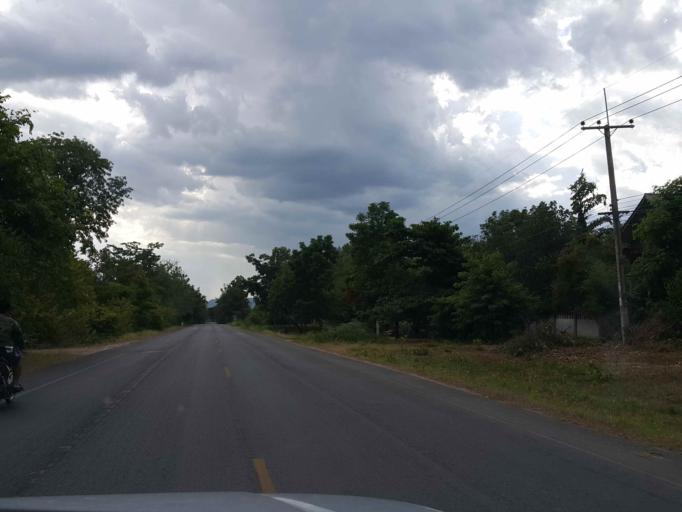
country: TH
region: Lampang
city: Thoen
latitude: 17.6499
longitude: 99.2704
